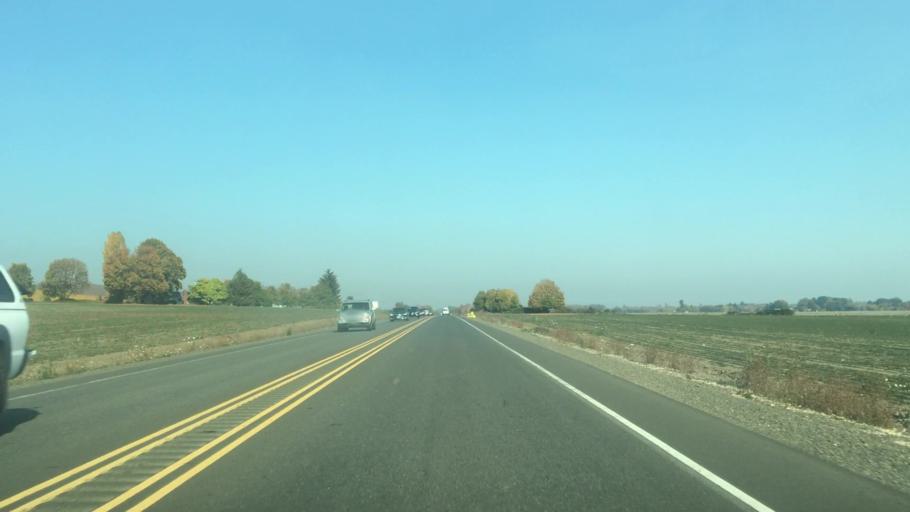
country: US
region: Oregon
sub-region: Yamhill County
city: Amity
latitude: 45.1343
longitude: -123.2935
